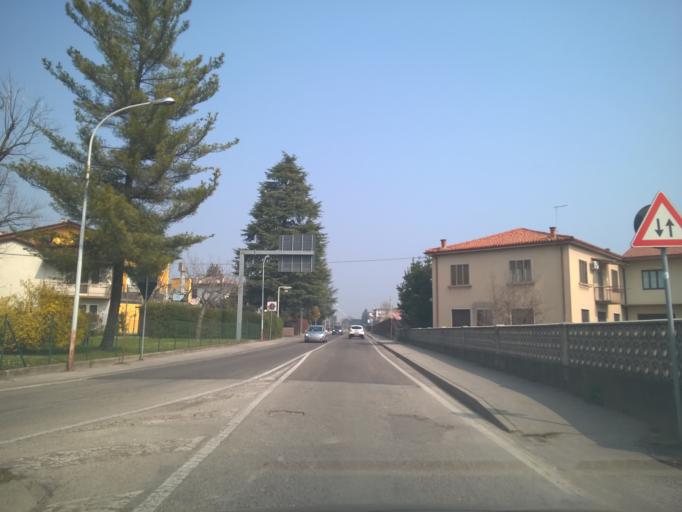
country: IT
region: Veneto
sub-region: Provincia di Vicenza
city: Thiene
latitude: 45.6973
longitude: 11.4838
